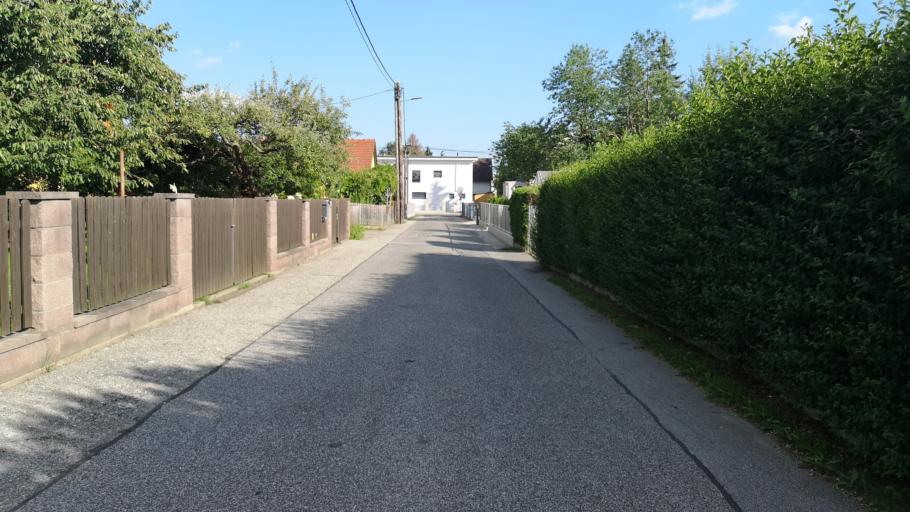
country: AT
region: Styria
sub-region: Politischer Bezirk Graz-Umgebung
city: Feldkirchen bei Graz
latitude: 47.0211
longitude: 15.4640
